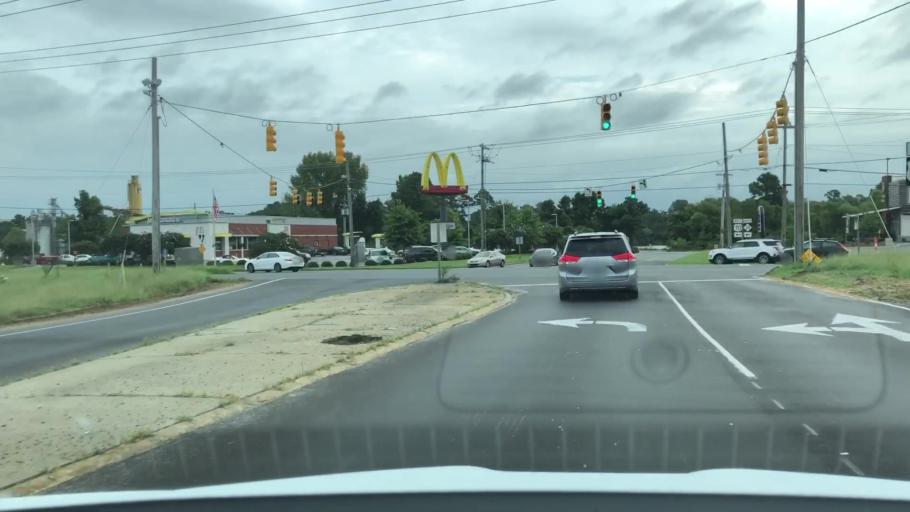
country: US
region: North Carolina
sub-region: Lenoir County
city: Kinston
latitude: 35.2369
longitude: -77.5739
